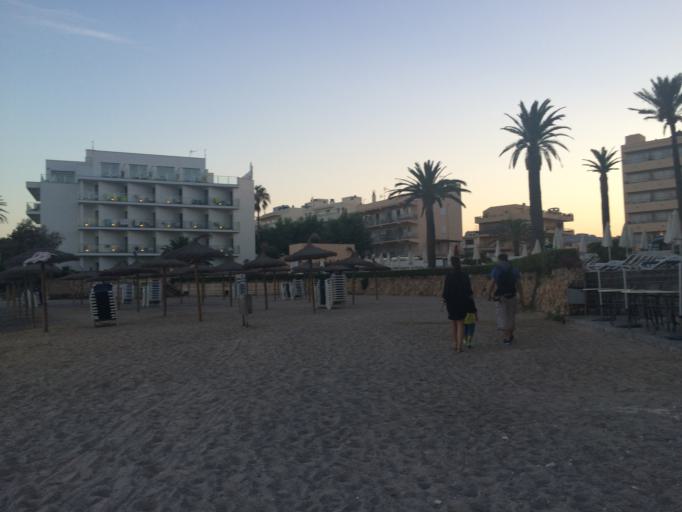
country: ES
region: Balearic Islands
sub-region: Illes Balears
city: Son Servera
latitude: 39.6120
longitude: 3.3914
